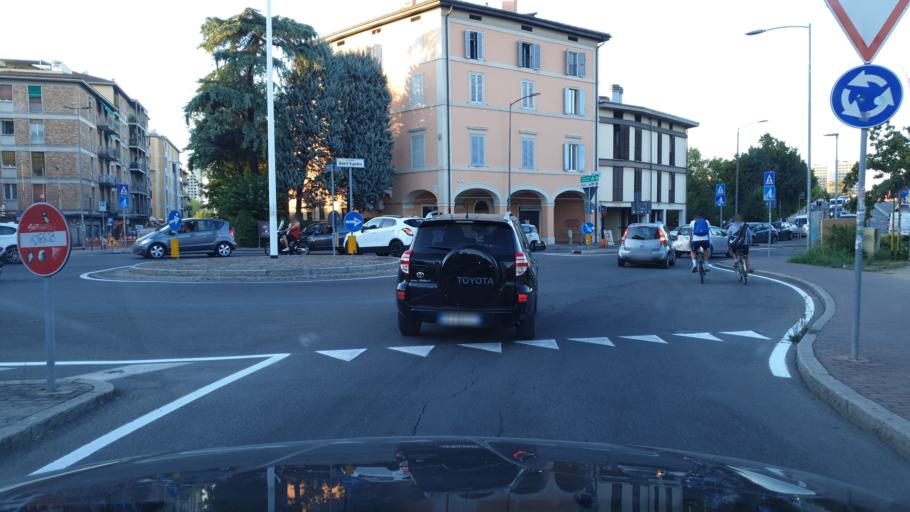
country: IT
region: Emilia-Romagna
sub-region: Provincia di Bologna
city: Bologna
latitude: 44.4995
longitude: 11.3594
